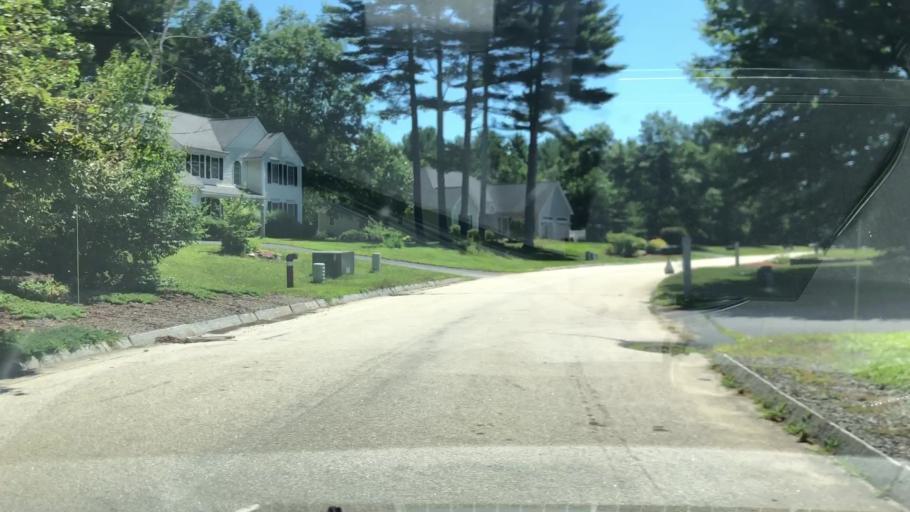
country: US
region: New Hampshire
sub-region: Hillsborough County
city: Milford
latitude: 42.8435
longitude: -71.5766
